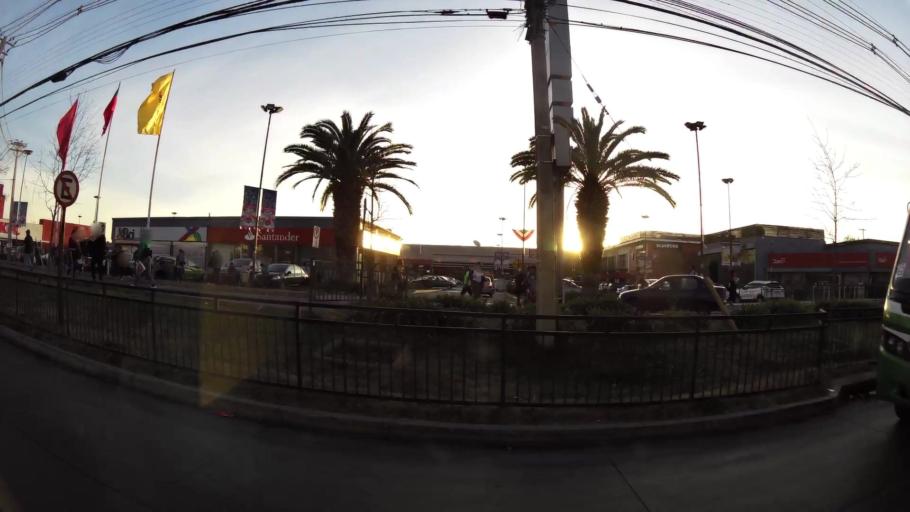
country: CL
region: Santiago Metropolitan
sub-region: Provincia de Cordillera
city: Puente Alto
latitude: -33.6011
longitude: -70.5777
